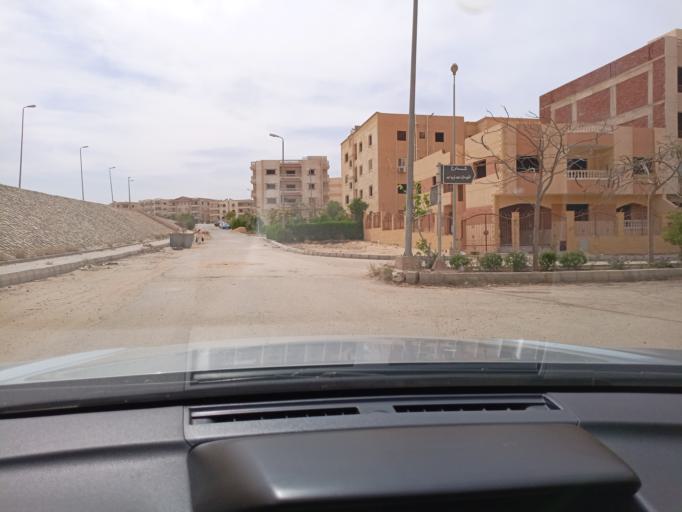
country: EG
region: Muhafazat al Qalyubiyah
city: Al Khankah
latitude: 30.2432
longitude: 31.4920
